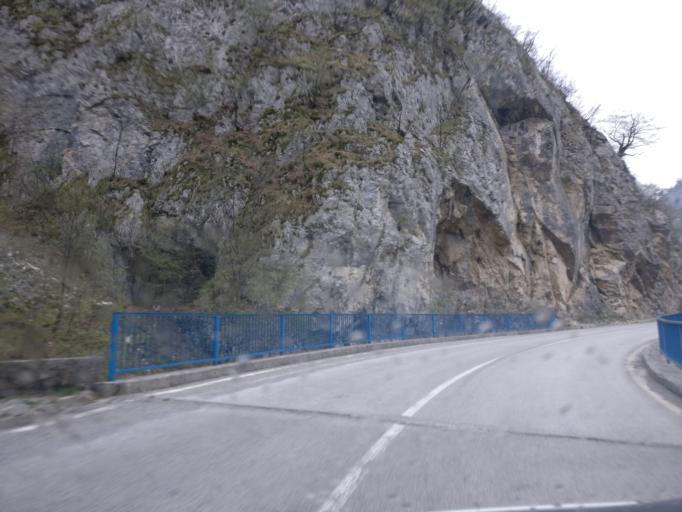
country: ME
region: Opstina Pluzine
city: Pluzine
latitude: 43.2243
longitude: 18.8473
